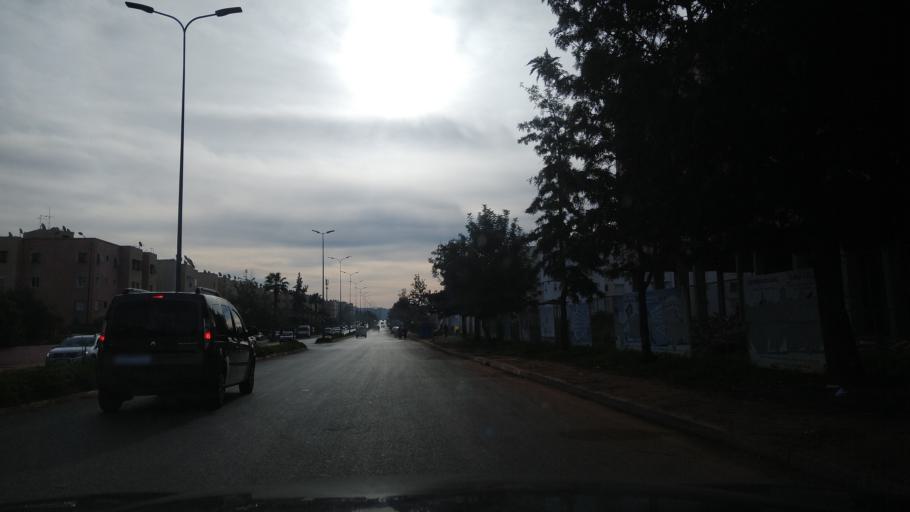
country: MA
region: Rabat-Sale-Zemmour-Zaer
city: Sale
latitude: 33.9958
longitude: -6.7465
